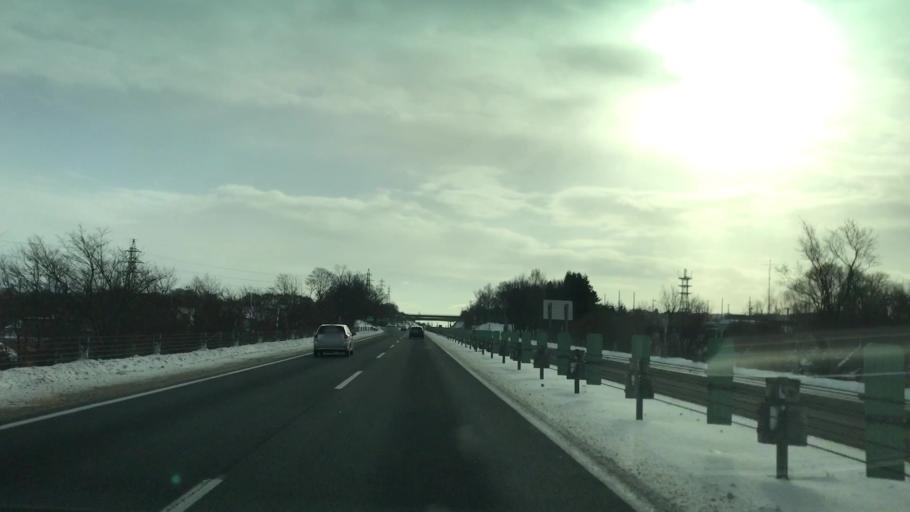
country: JP
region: Hokkaido
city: Kitahiroshima
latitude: 42.9701
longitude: 141.4878
